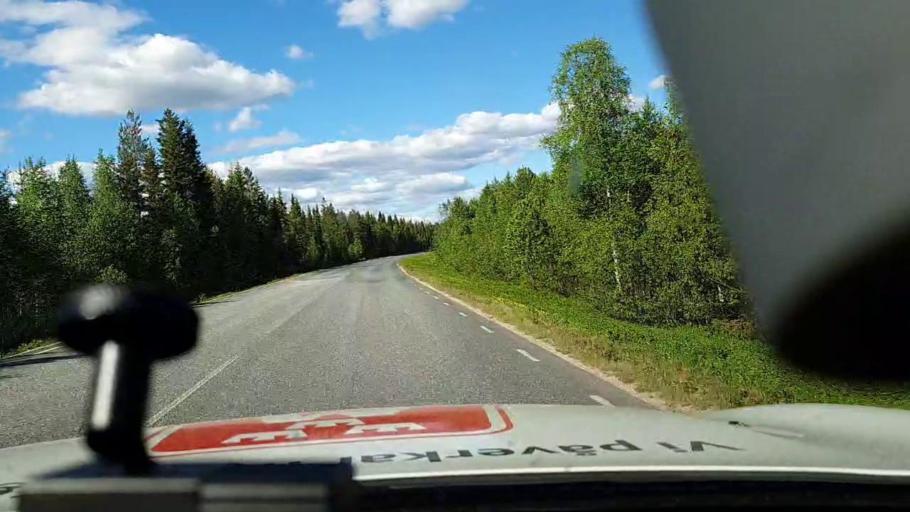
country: FI
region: Lapland
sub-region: Torniolaakso
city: Ylitornio
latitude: 66.3223
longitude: 23.6220
